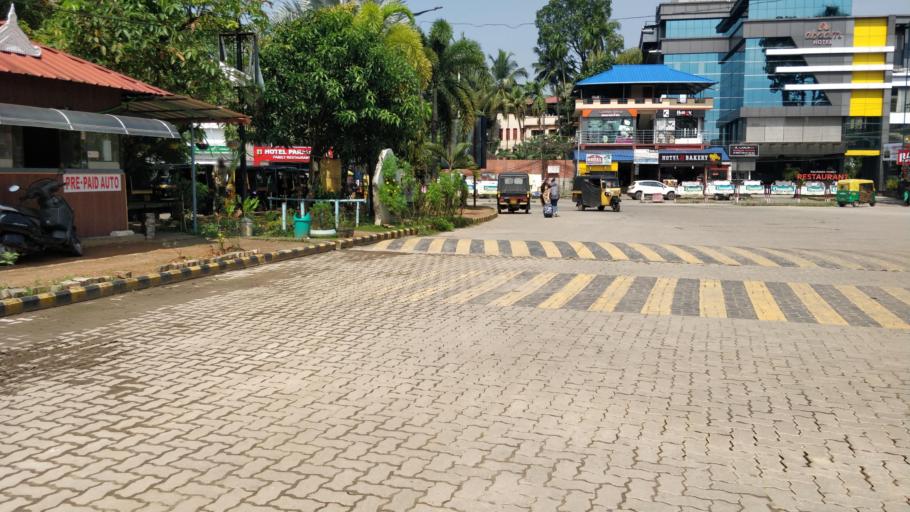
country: IN
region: Kerala
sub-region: Ernakulam
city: Cochin
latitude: 9.9696
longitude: 76.3212
